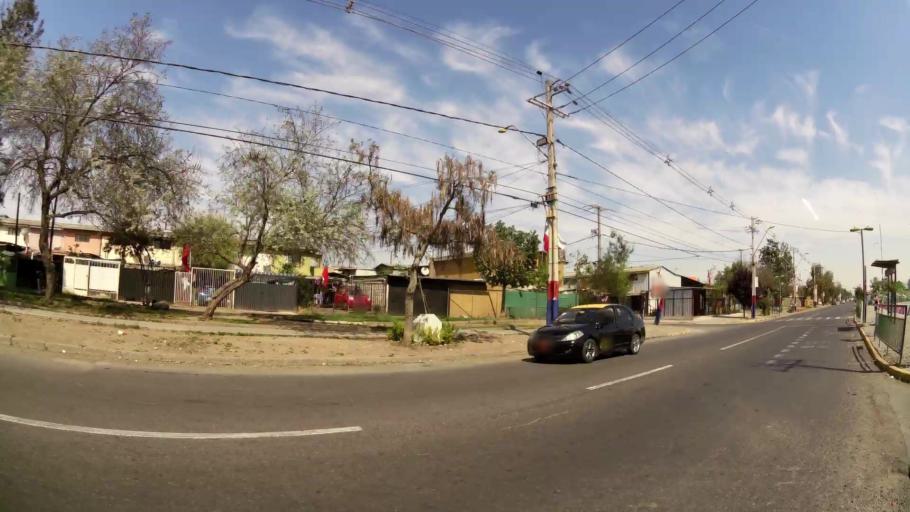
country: CL
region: Santiago Metropolitan
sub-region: Provincia de Santiago
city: La Pintana
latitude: -33.5609
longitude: -70.6403
